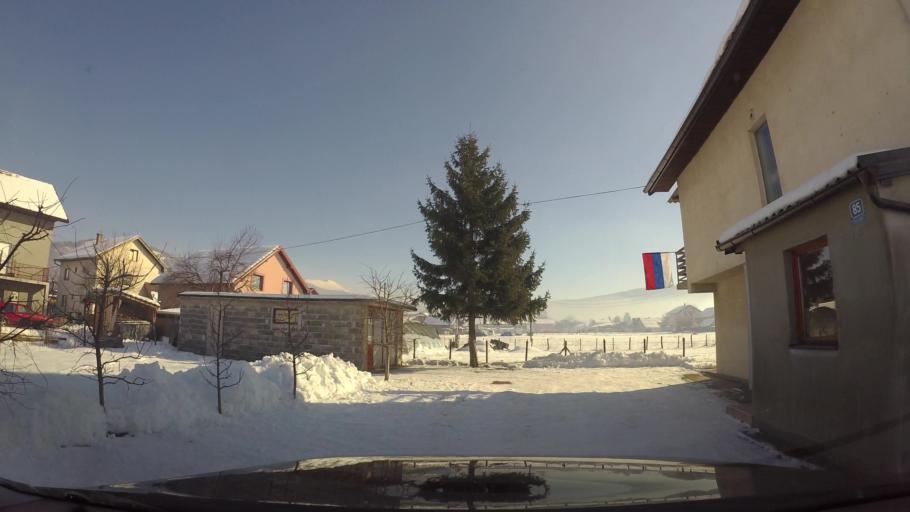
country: BA
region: Federation of Bosnia and Herzegovina
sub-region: Kanton Sarajevo
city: Sarajevo
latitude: 43.7992
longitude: 18.3438
